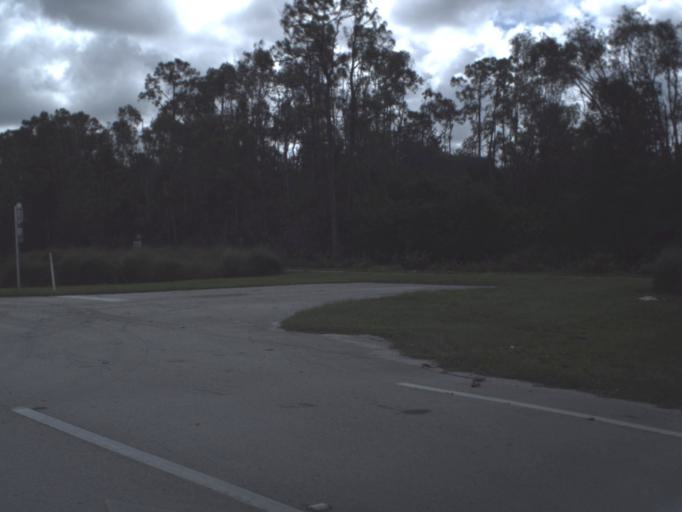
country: US
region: Florida
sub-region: Lee County
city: Fort Myers
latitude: 26.6364
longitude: -81.8077
